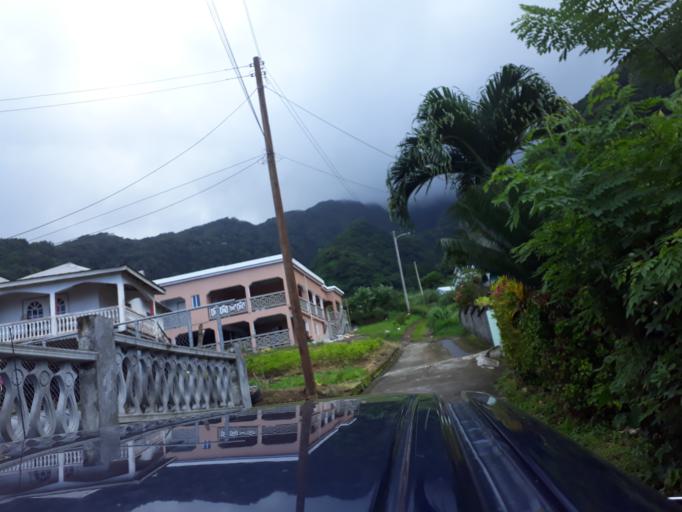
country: VC
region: Charlotte
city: Georgetown
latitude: 13.3775
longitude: -61.1700
